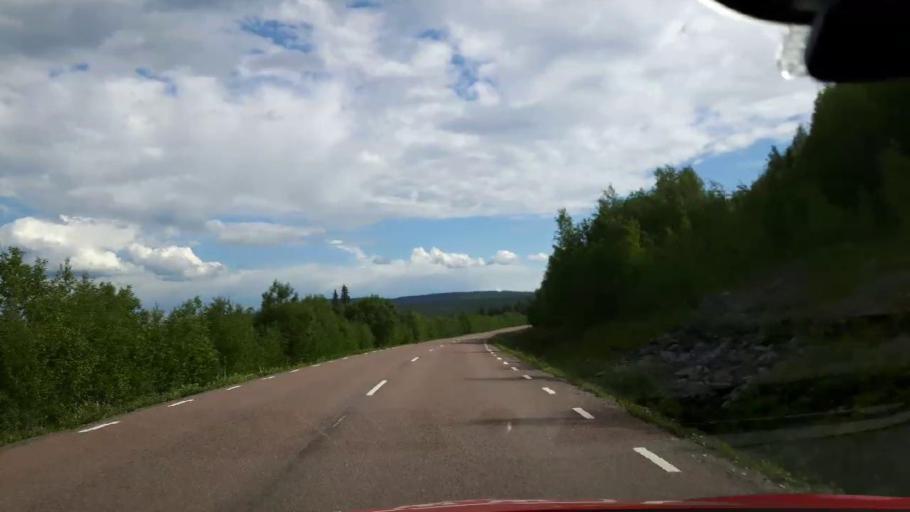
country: SE
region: Jaemtland
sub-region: Krokoms Kommun
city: Valla
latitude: 63.9255
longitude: 14.2132
